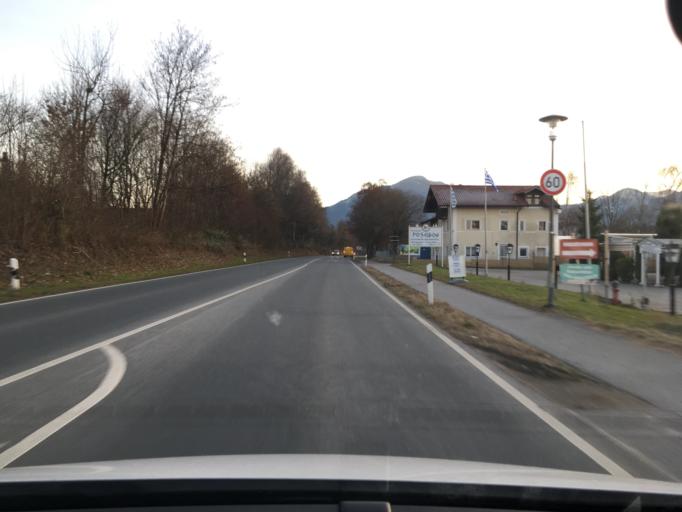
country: DE
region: Bavaria
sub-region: Upper Bavaria
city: Raubling
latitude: 47.7686
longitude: 12.1063
